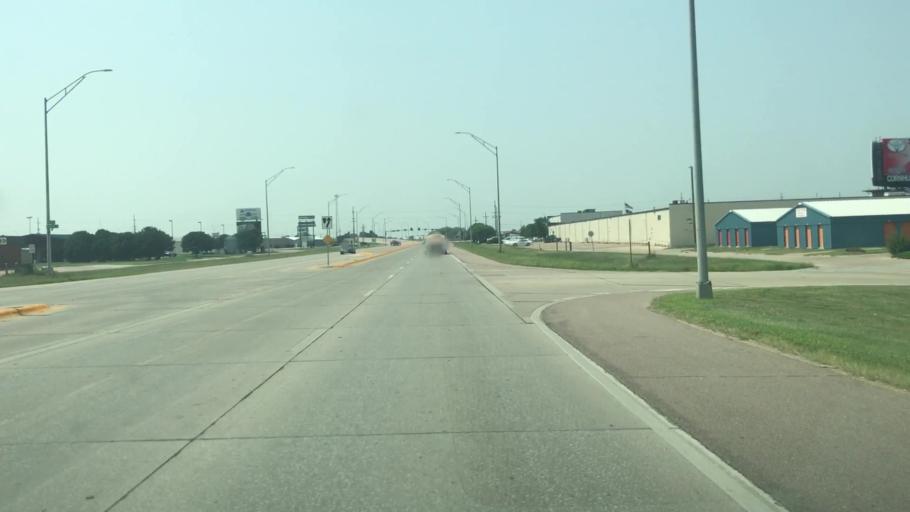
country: US
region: Nebraska
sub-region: Hall County
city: Grand Island
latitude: 40.9157
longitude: -98.3737
